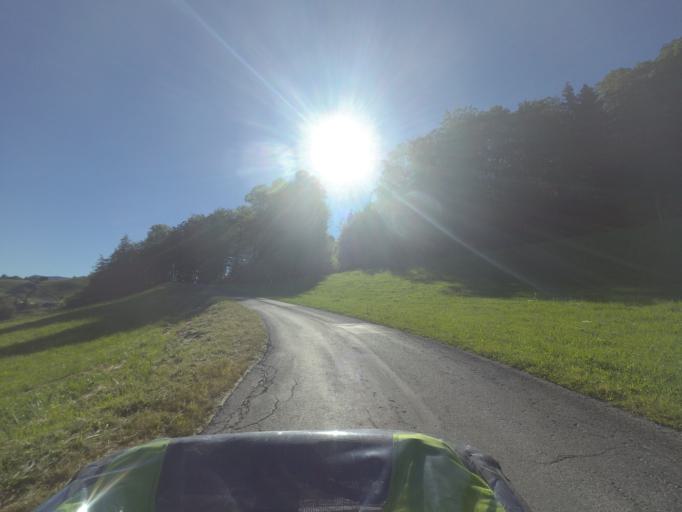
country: AT
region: Salzburg
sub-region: Politischer Bezirk Hallein
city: Hallein
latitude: 47.6583
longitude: 13.0937
